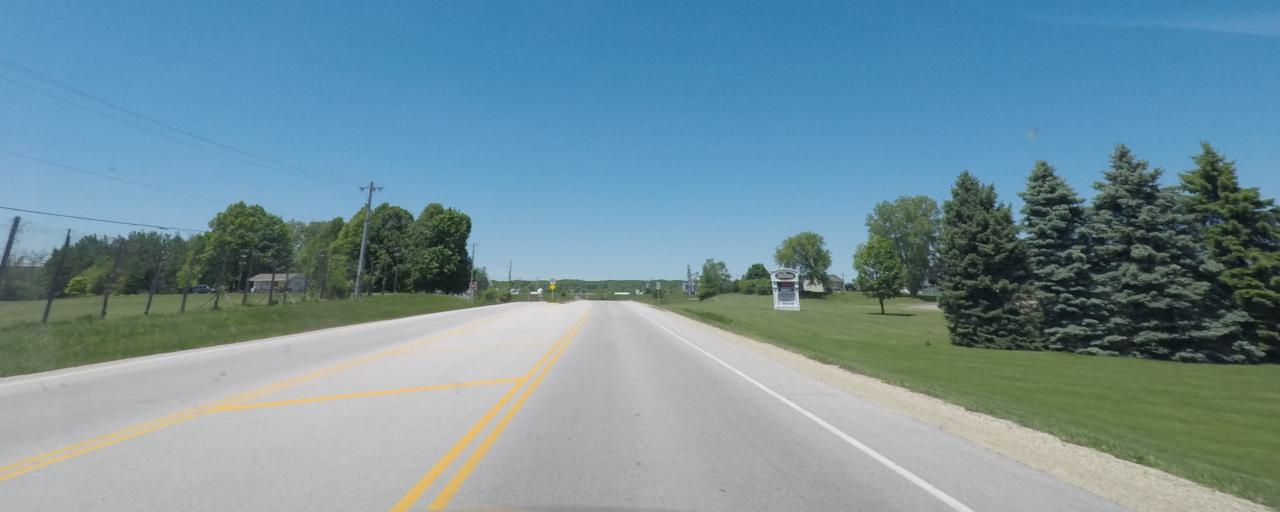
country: US
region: Wisconsin
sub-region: Washington County
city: West Bend
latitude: 43.4538
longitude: -88.1987
